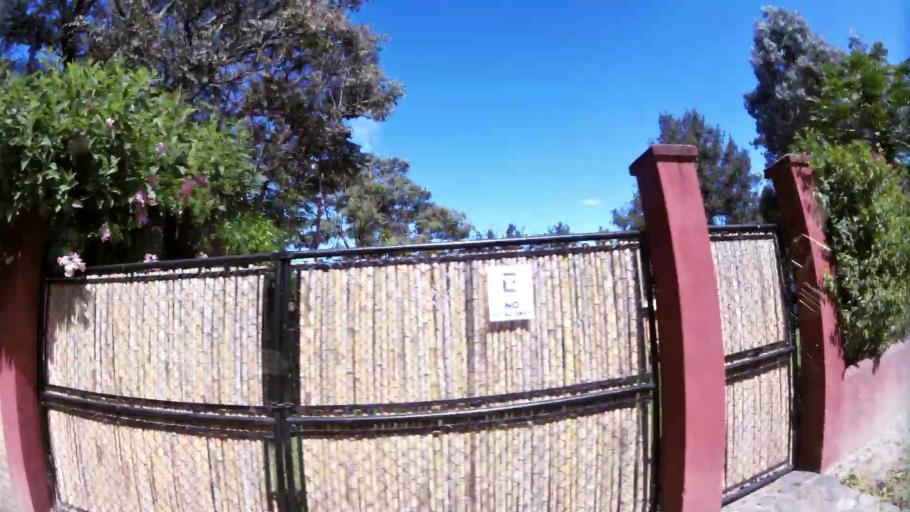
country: GT
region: Solola
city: Panajachel
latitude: 14.7383
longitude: -91.1595
